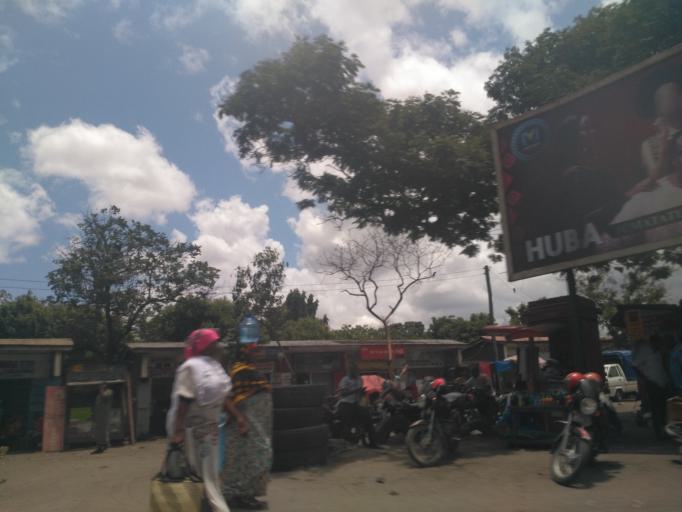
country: TZ
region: Dar es Salaam
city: Dar es Salaam
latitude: -6.8634
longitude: 39.2631
